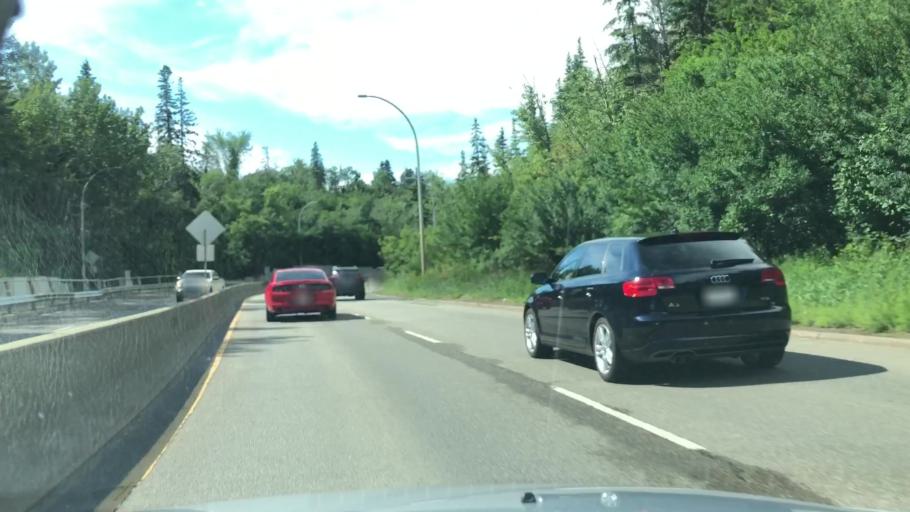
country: CA
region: Alberta
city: Edmonton
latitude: 53.5460
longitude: -113.5433
